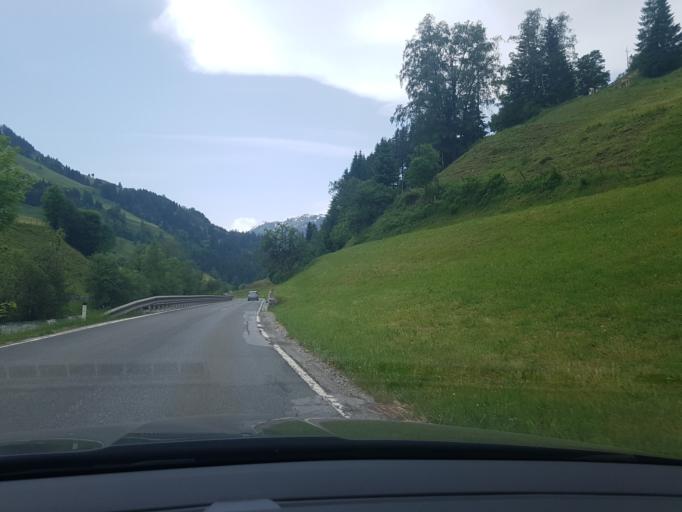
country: AT
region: Salzburg
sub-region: Politischer Bezirk Sankt Johann im Pongau
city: Sankt Johann im Pongau
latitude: 47.2758
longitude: 13.2135
